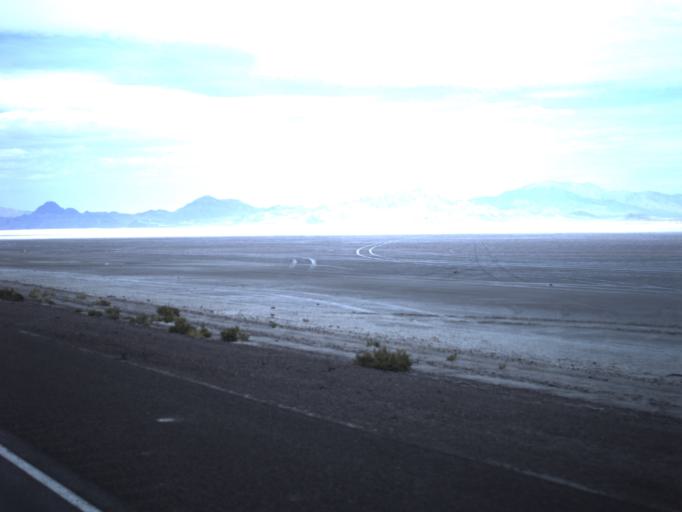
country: US
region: Utah
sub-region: Tooele County
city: Wendover
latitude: 40.7378
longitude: -113.7732
